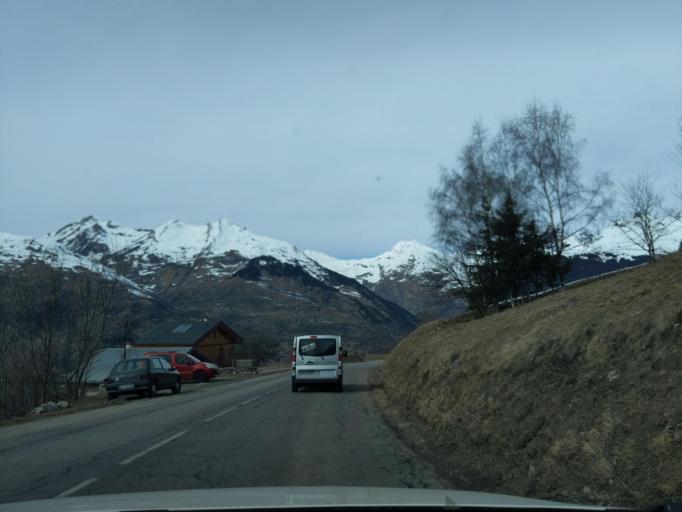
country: FR
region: Rhone-Alpes
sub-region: Departement de la Savoie
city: Bourg-Saint-Maurice
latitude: 45.5986
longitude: 6.7809
